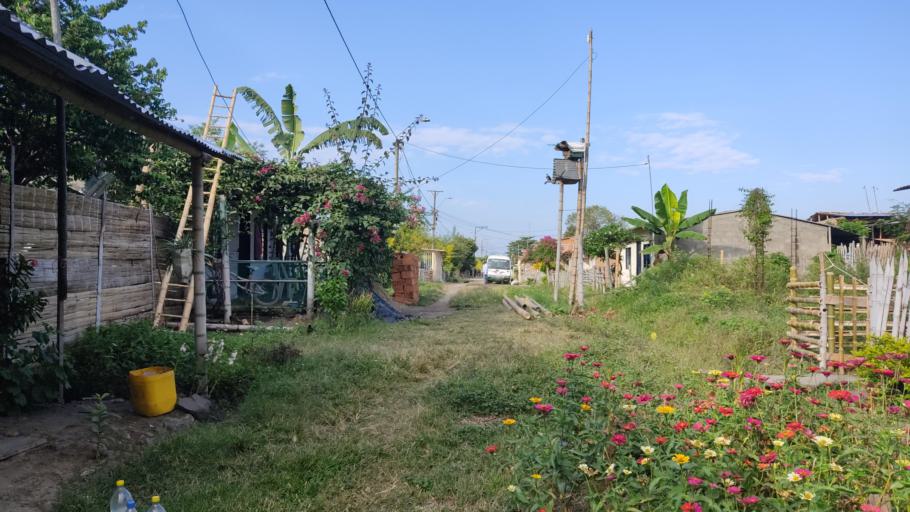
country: CO
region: Valle del Cauca
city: Jamundi
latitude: 3.1308
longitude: -76.5563
